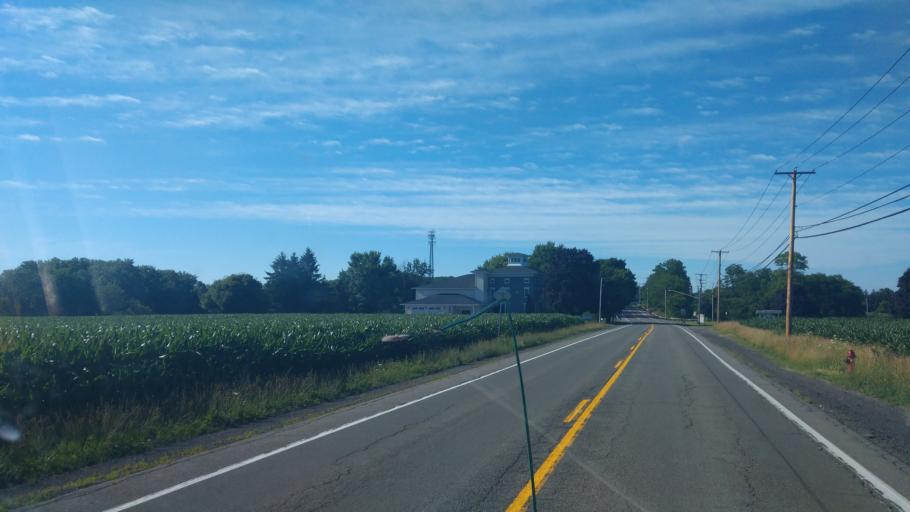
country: US
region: New York
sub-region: Wayne County
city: Lyons
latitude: 43.0520
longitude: -76.9936
